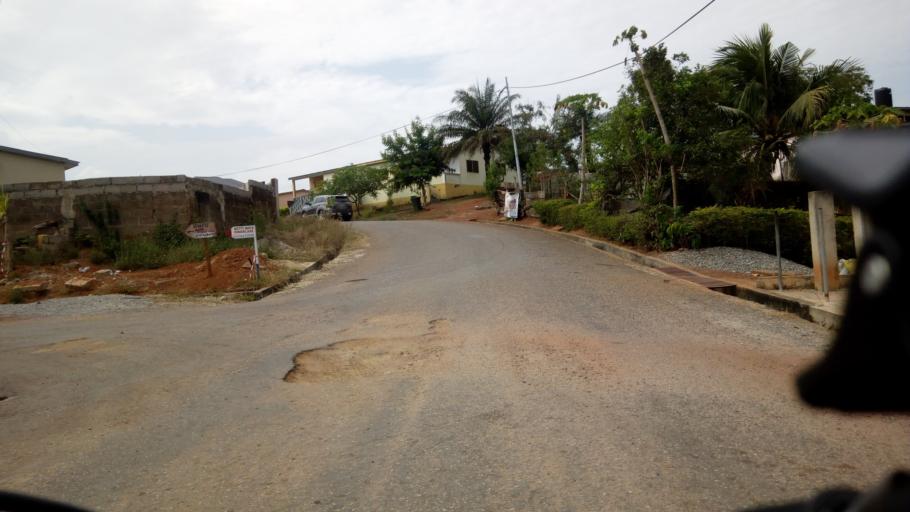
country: GH
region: Central
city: Cape Coast
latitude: 5.1072
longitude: -1.2770
